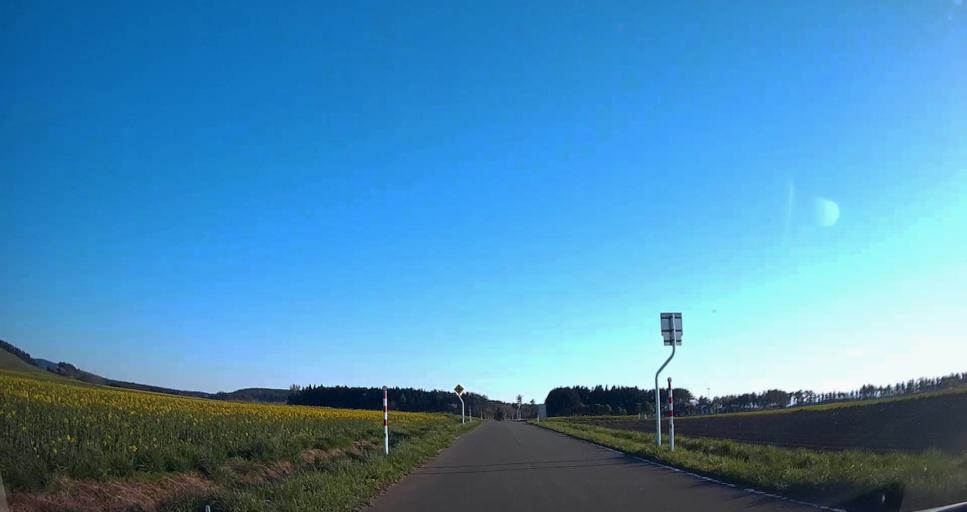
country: JP
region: Aomori
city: Mutsu
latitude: 41.1151
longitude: 141.2739
